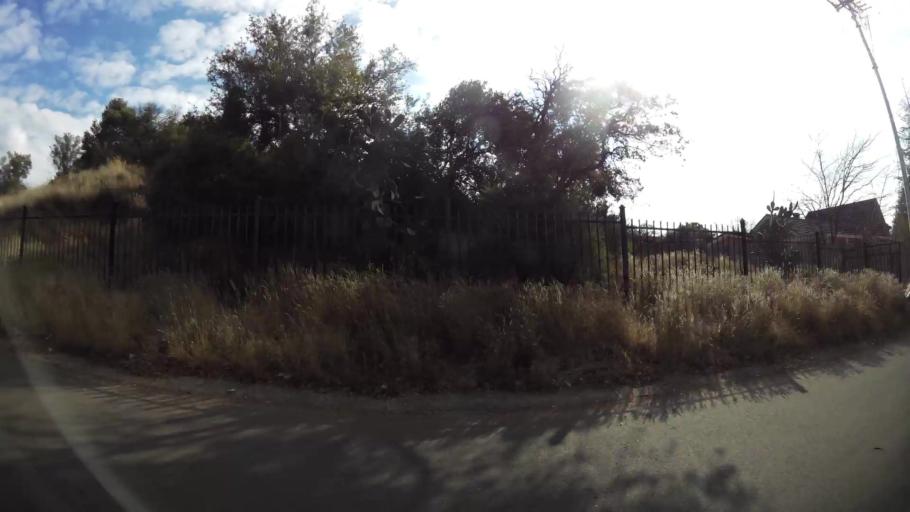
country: ZA
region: Orange Free State
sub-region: Mangaung Metropolitan Municipality
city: Bloemfontein
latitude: -29.0780
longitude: 26.2399
